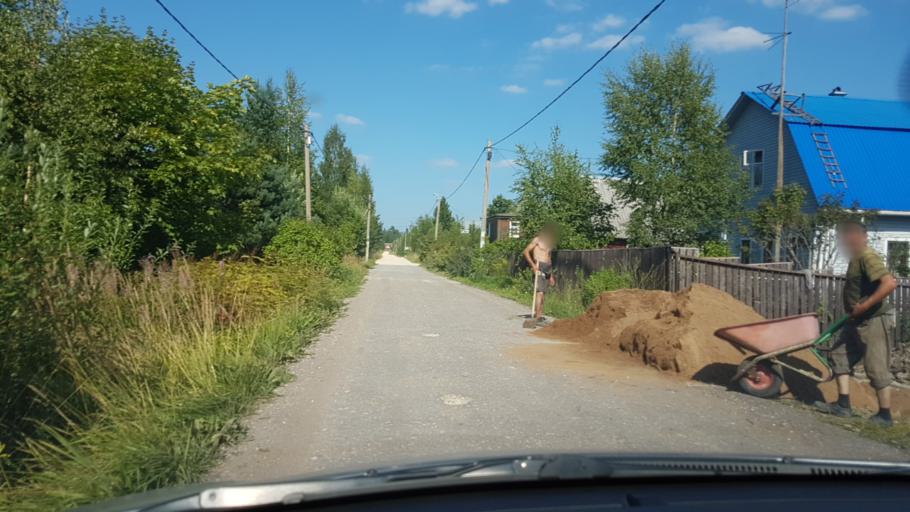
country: RU
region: Leningrad
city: Vyritsa
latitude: 59.4502
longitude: 30.2966
